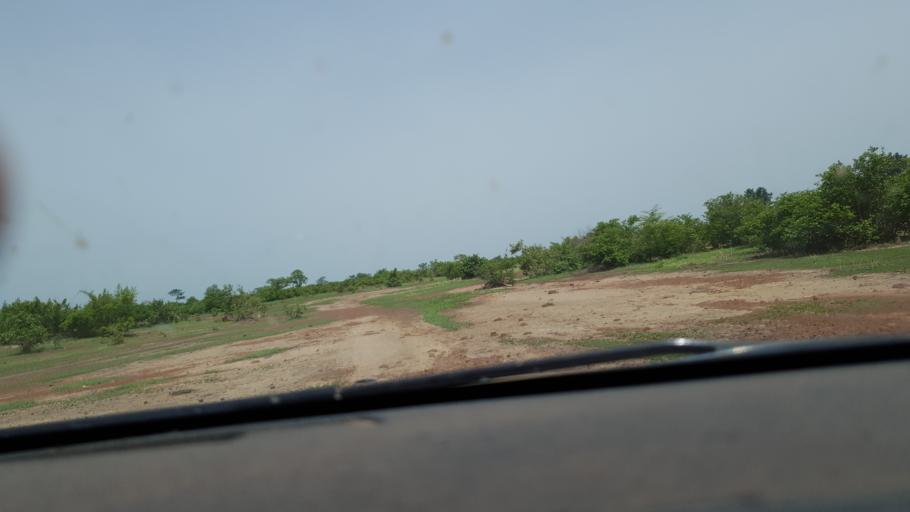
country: ML
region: Koulikoro
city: Koulikoro
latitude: 12.6654
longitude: -7.2265
